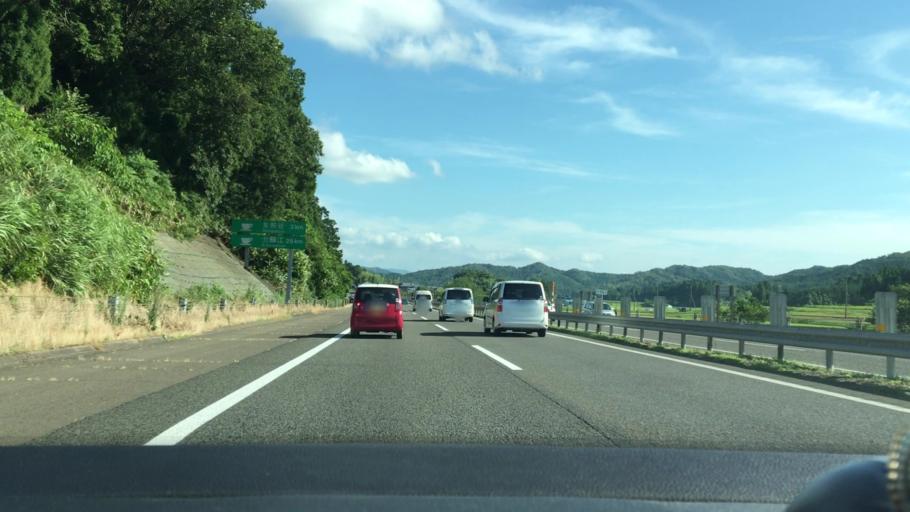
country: JP
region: Fukui
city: Maruoka
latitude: 36.1980
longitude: 136.2868
